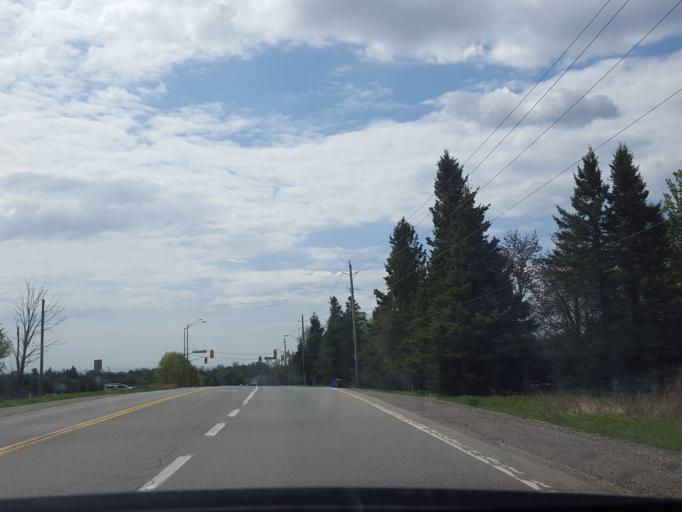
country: CA
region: Ontario
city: Oshawa
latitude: 43.9233
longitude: -78.7073
